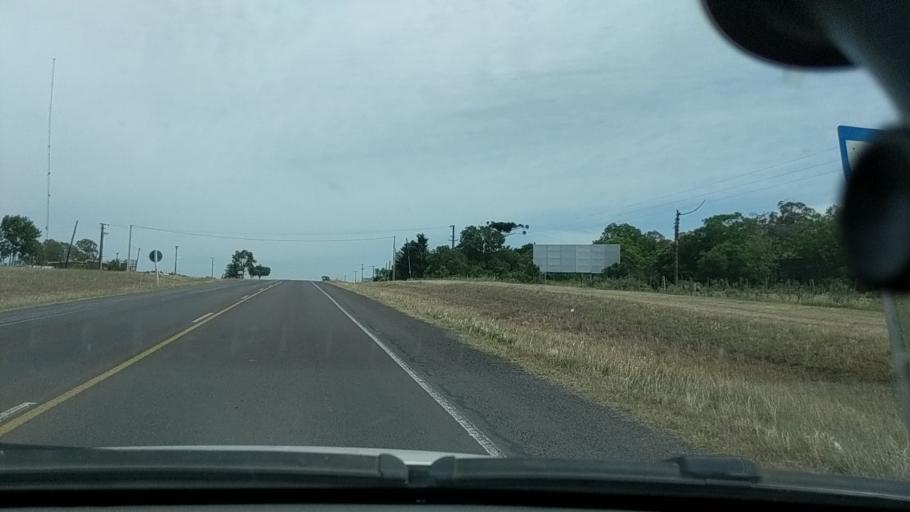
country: UY
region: Durazno
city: Durazno
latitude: -33.4494
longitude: -56.4740
